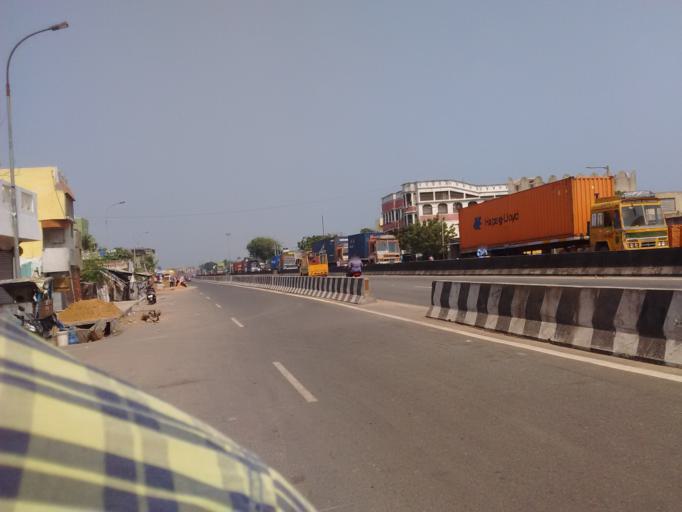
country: IN
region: Tamil Nadu
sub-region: Thiruvallur
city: Tiruvottiyur
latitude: 13.1588
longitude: 80.3057
